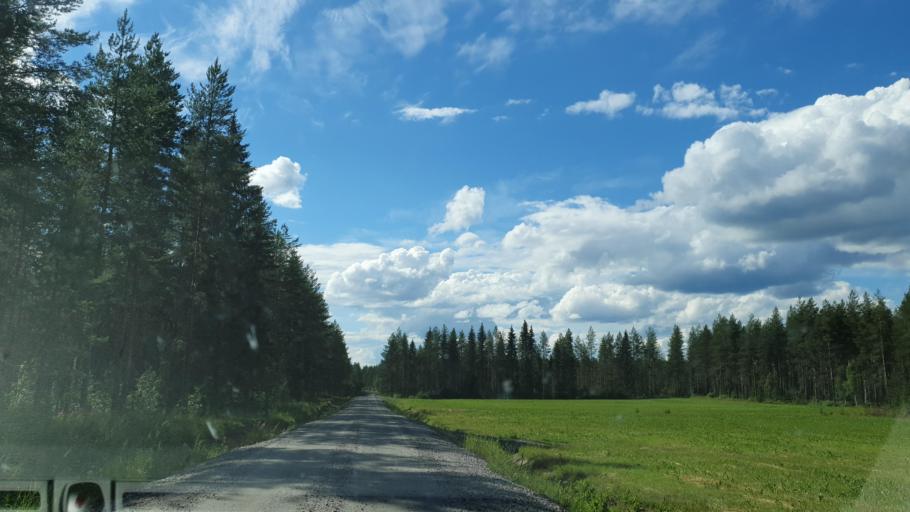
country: FI
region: Kainuu
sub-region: Kehys-Kainuu
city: Kuhmo
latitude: 64.1459
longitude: 29.7734
